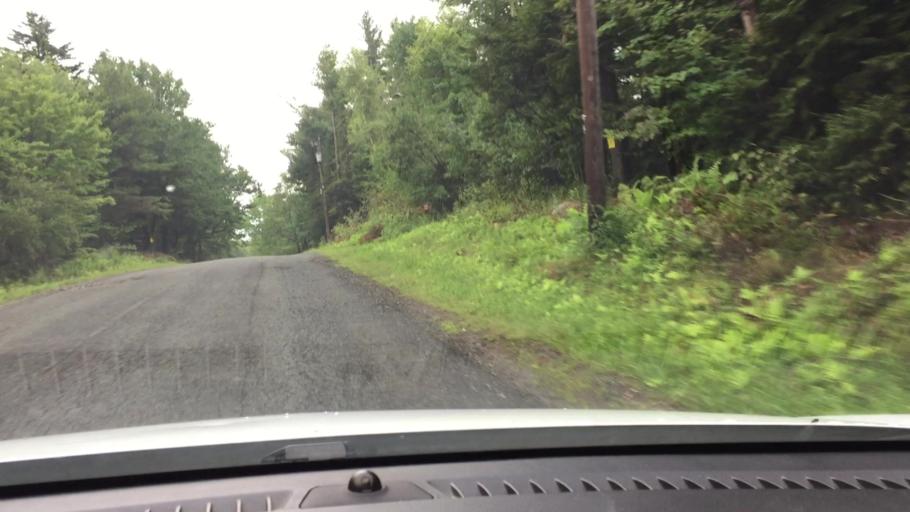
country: US
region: Massachusetts
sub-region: Berkshire County
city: Hinsdale
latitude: 42.4249
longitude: -73.0492
